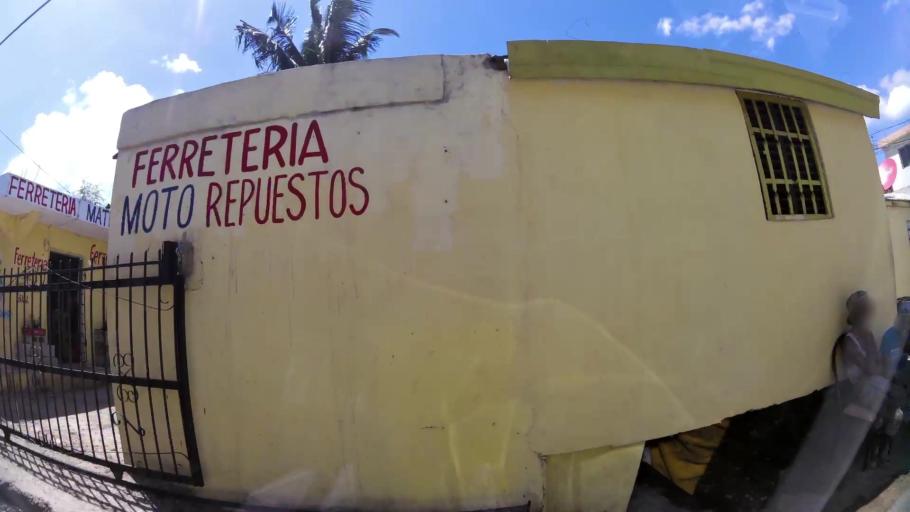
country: DO
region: San Cristobal
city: San Cristobal
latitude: 18.3995
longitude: -70.1113
